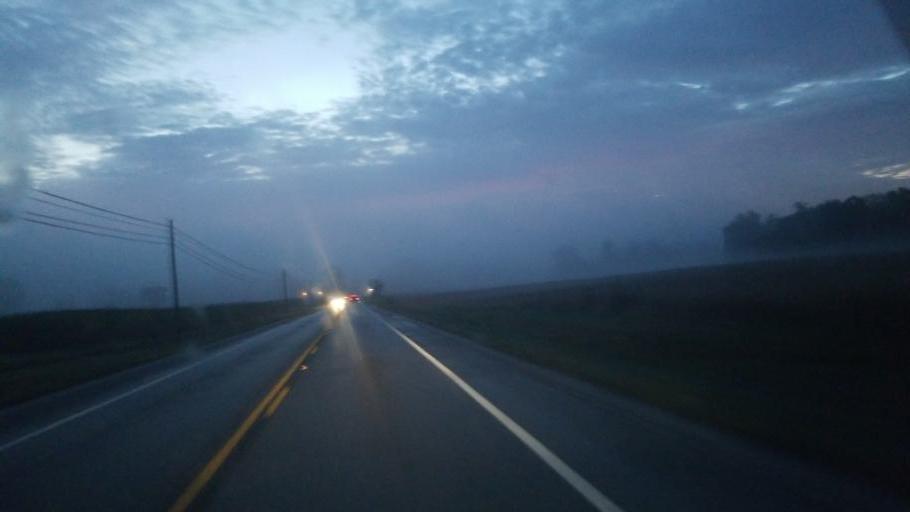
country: US
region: Ohio
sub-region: Wayne County
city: Apple Creek
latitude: 40.7562
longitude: -81.8571
